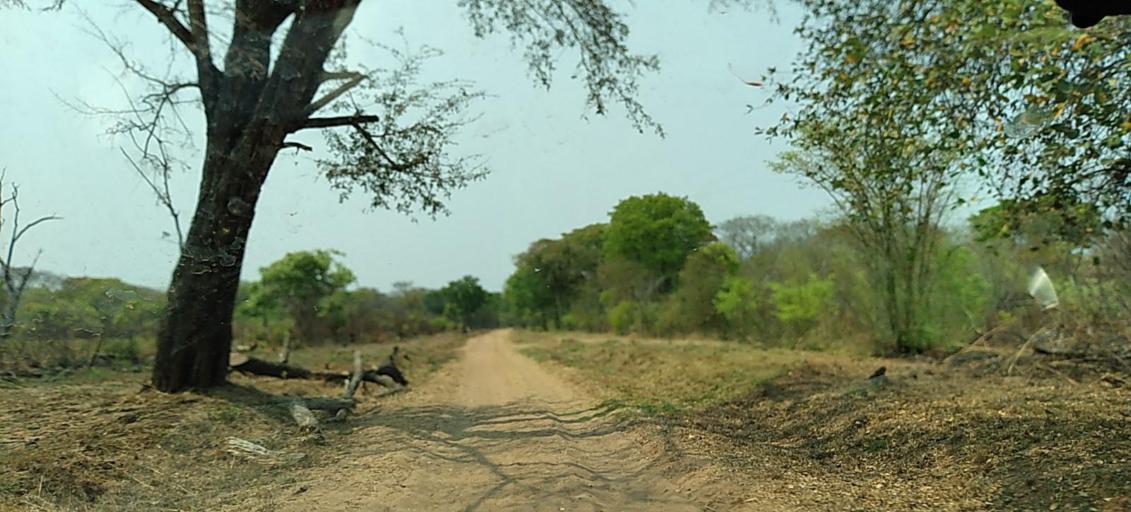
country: ZM
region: Western
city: Lukulu
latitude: -13.9895
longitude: 23.2308
